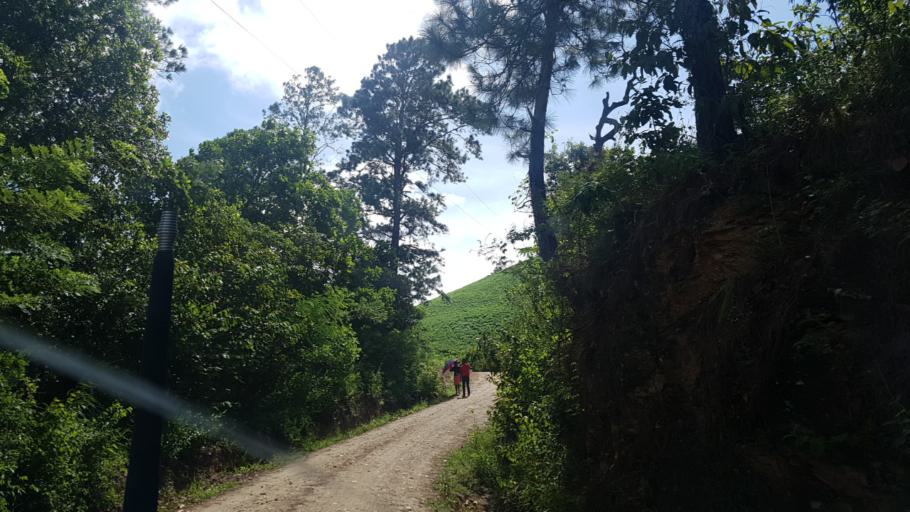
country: NI
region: Nueva Segovia
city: Ciudad Antigua
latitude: 13.6450
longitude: -86.2755
